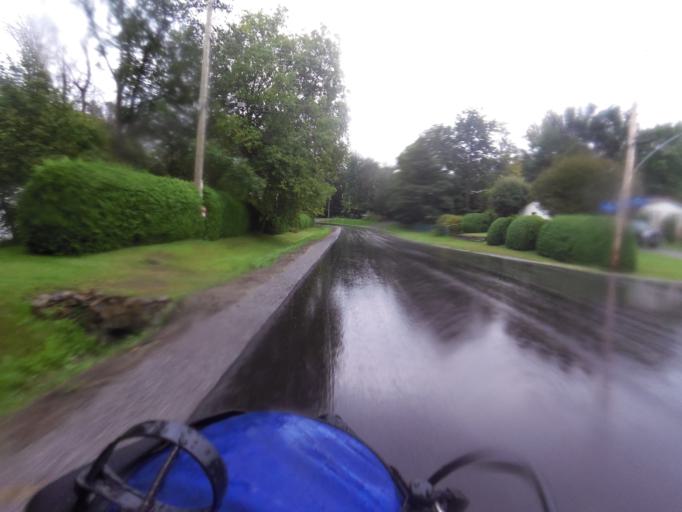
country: CA
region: Ontario
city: Ottawa
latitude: 45.2359
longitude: -75.4657
